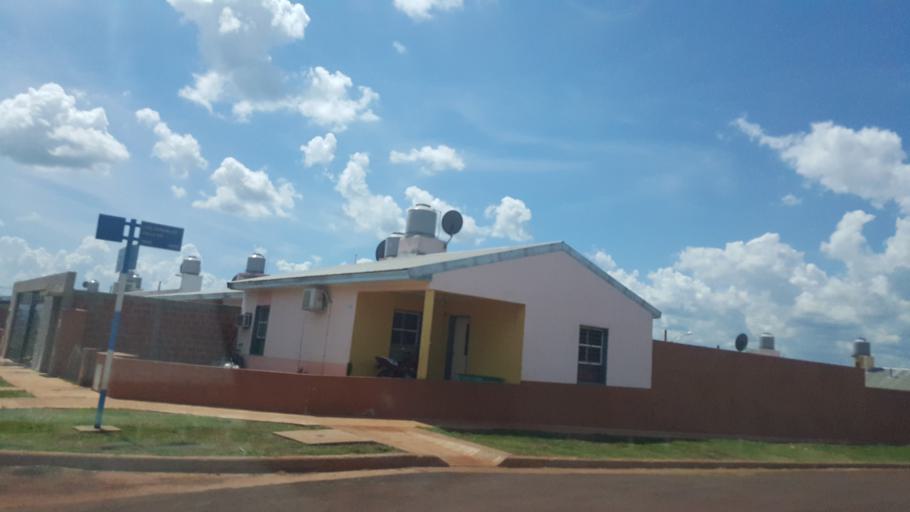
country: AR
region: Misiones
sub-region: Departamento de Capital
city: Posadas
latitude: -27.4068
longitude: -55.9791
